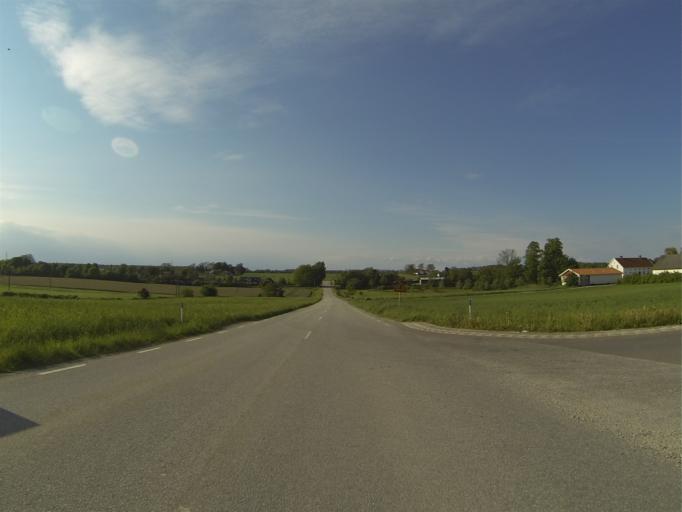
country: SE
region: Skane
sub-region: Lunds Kommun
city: Lund
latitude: 55.7105
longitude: 13.2989
